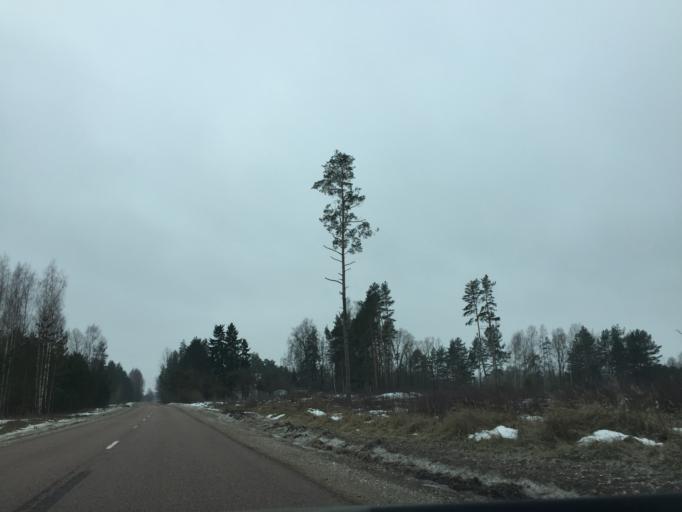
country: LV
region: Olaine
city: Olaine
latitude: 56.6374
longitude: 23.9364
